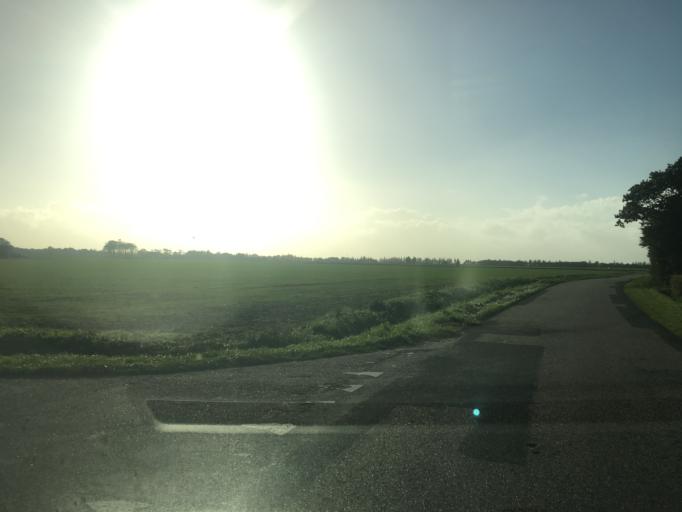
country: DK
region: South Denmark
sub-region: Tonder Kommune
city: Tonder
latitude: 54.9771
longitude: 8.8558
